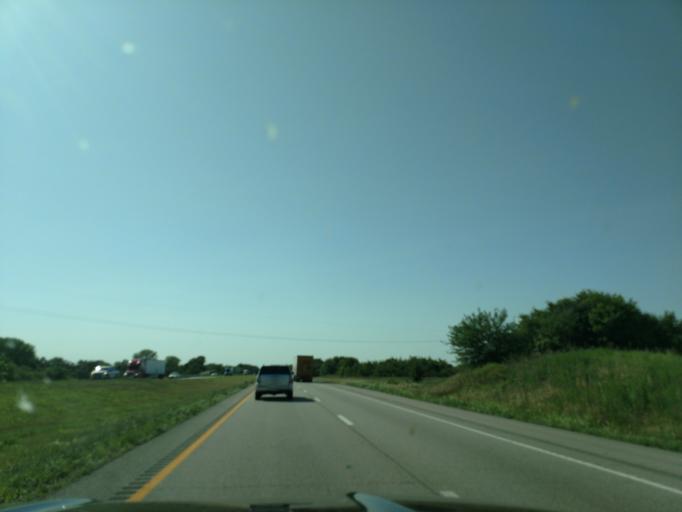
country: US
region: Missouri
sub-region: Andrew County
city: Savannah
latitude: 39.8888
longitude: -94.8602
